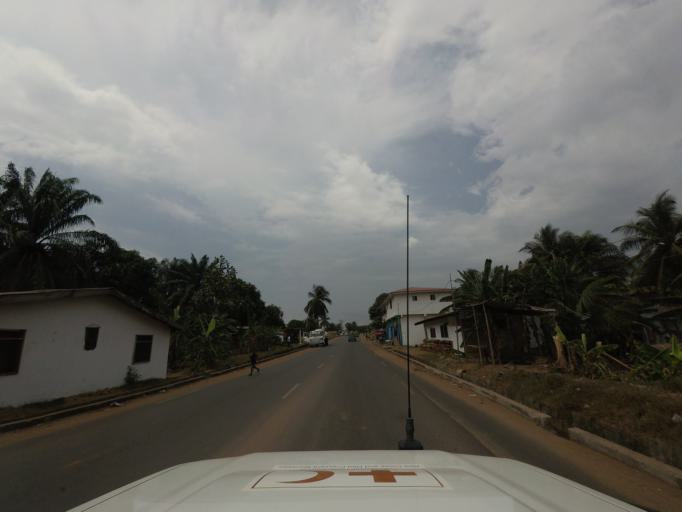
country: LR
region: Montserrado
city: Monrovia
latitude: 6.2864
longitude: -10.6809
